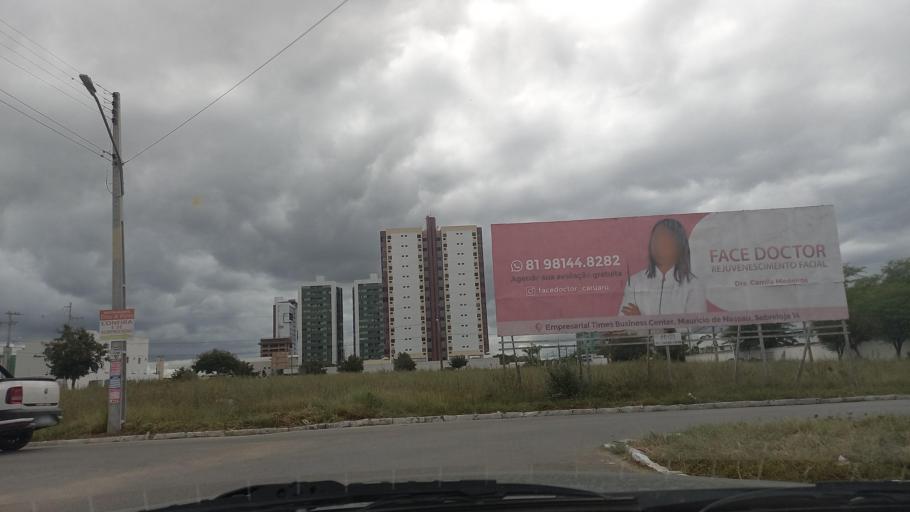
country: BR
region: Pernambuco
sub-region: Caruaru
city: Caruaru
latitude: -8.2642
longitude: -35.9662
